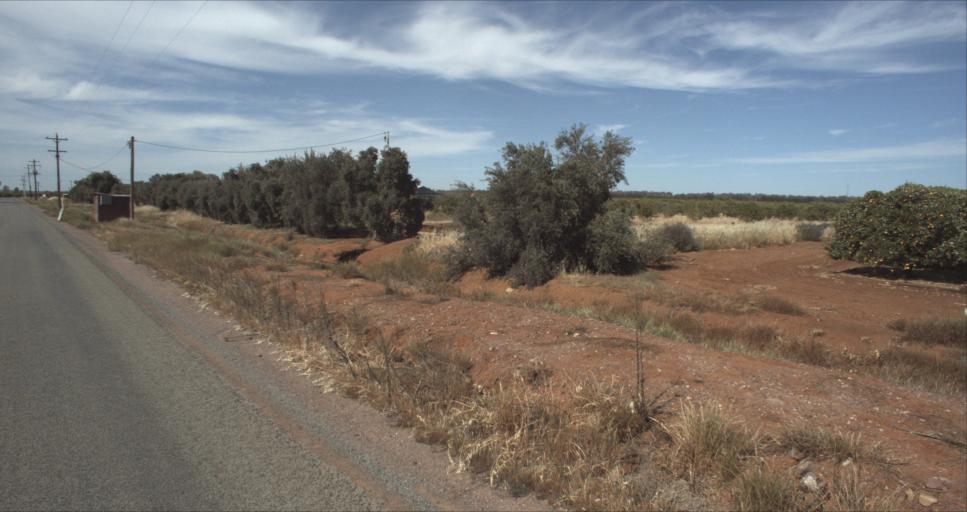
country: AU
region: New South Wales
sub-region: Leeton
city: Leeton
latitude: -34.5842
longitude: 146.4711
